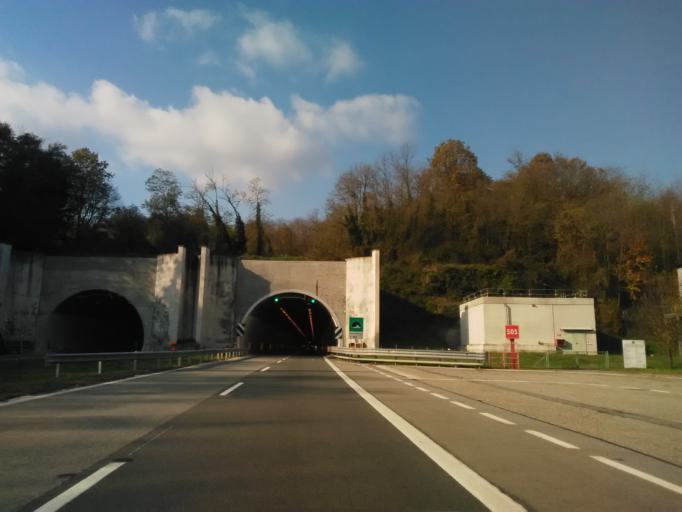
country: IT
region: Piedmont
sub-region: Provincia di Vercelli
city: Alice Castello
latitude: 45.3854
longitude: 8.0486
